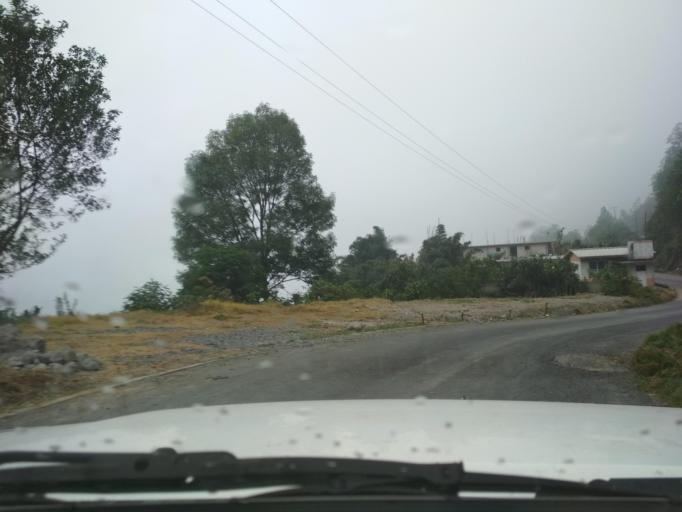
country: MX
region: Veracruz
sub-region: La Perla
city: Metlac Hernandez (Metlac Primero)
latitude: 18.9512
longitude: -97.1660
